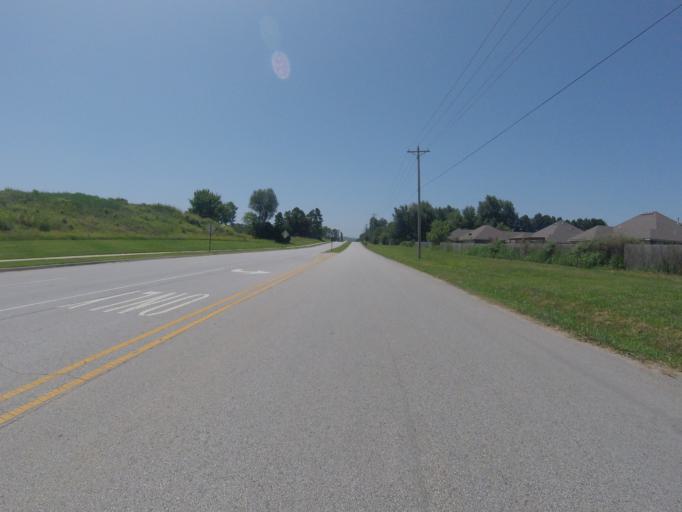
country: US
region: Arkansas
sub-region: Washington County
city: Farmington
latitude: 36.0846
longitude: -94.2173
